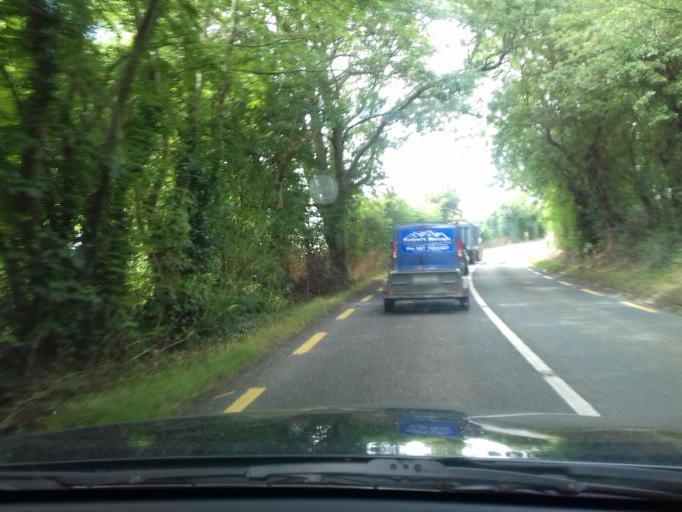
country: IE
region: Leinster
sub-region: Wicklow
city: Baltinglass
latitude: 52.9121
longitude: -6.7005
